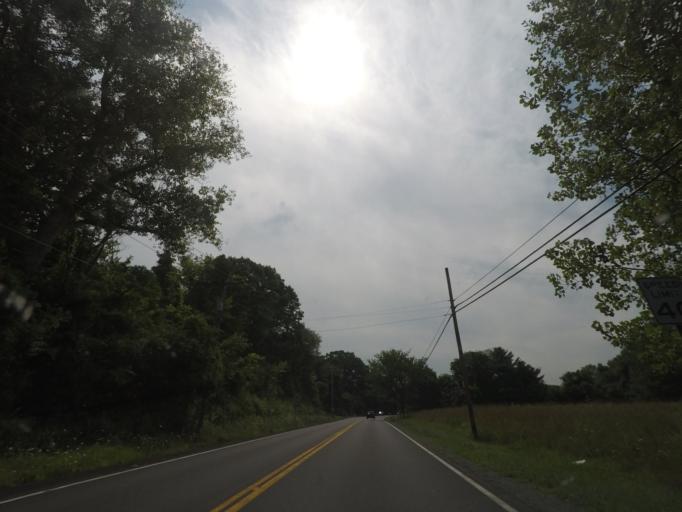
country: US
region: New York
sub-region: Saratoga County
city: Waterford
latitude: 42.7630
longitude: -73.6232
